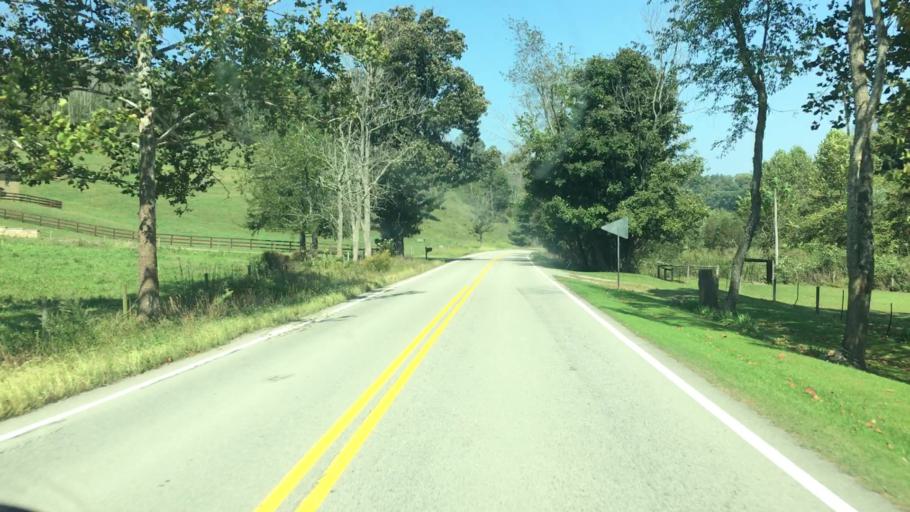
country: US
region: Pennsylvania
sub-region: Washington County
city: Washington
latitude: 40.0202
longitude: -80.3270
